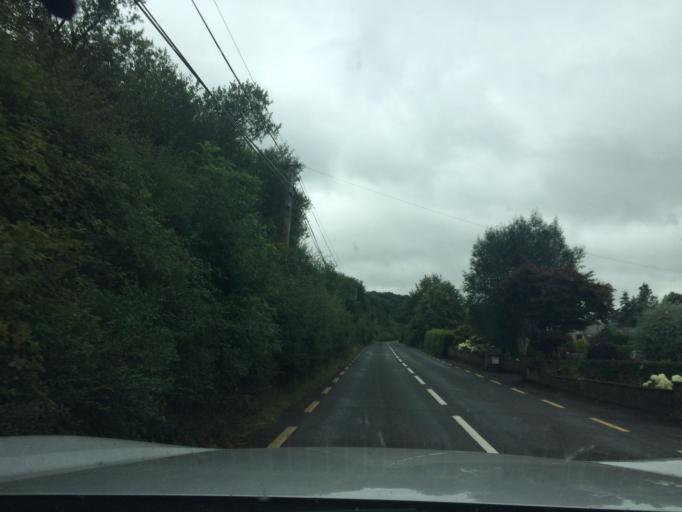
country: IE
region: Munster
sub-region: South Tipperary
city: Cluain Meala
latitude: 52.3343
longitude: -7.7276
